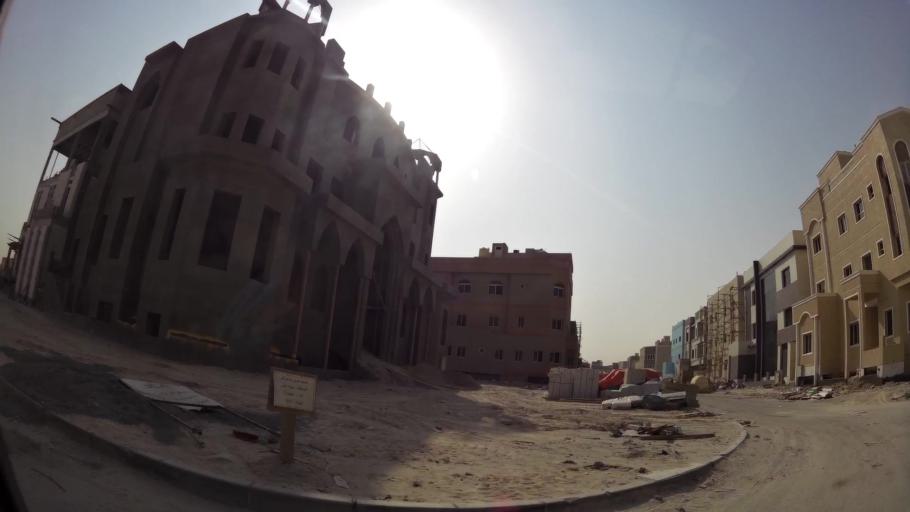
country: KW
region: Muhafazat al Jahra'
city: Al Jahra'
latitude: 29.3543
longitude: 47.7500
